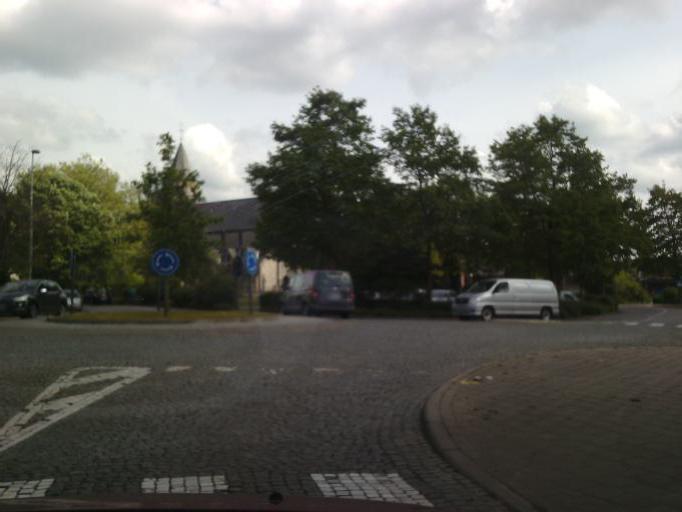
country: BE
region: Flanders
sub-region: Provincie Oost-Vlaanderen
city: Evergem
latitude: 51.0733
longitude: 3.6738
